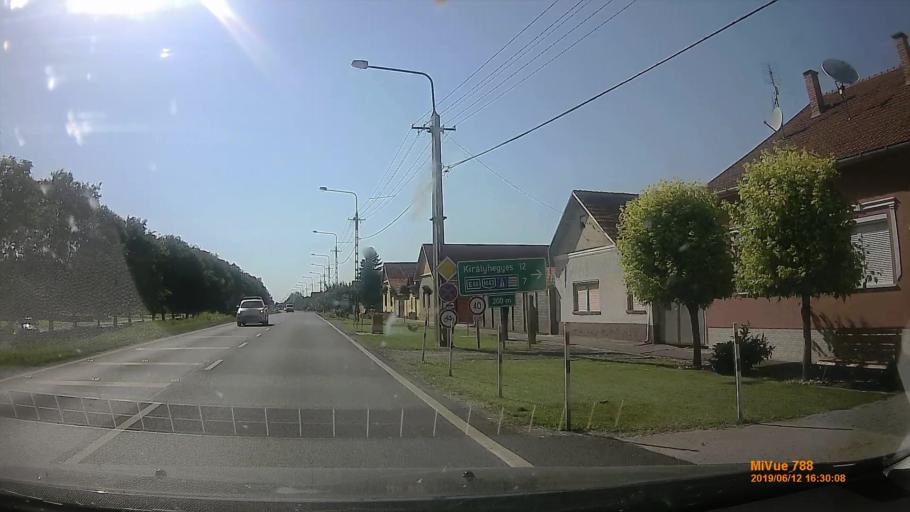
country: HU
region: Csongrad
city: Apatfalva
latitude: 46.1724
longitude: 20.5883
